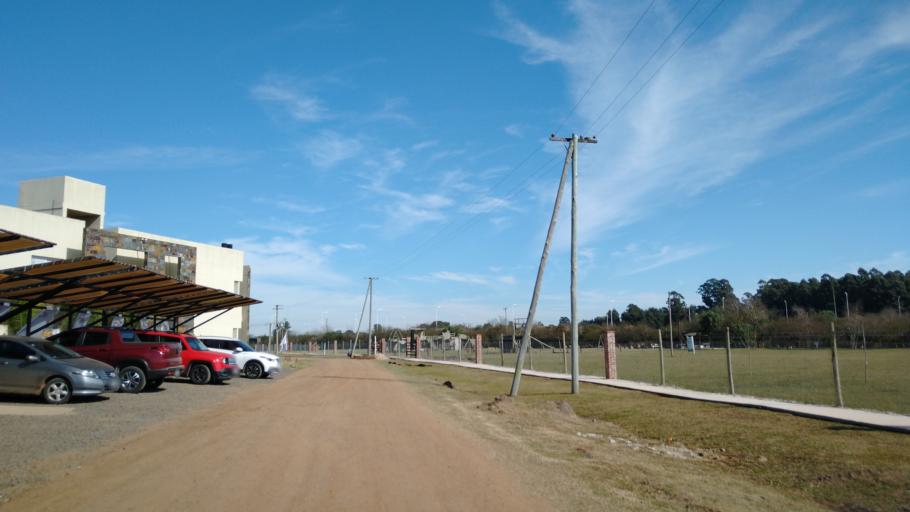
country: AR
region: Entre Rios
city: Chajari
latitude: -30.7413
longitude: -58.0129
